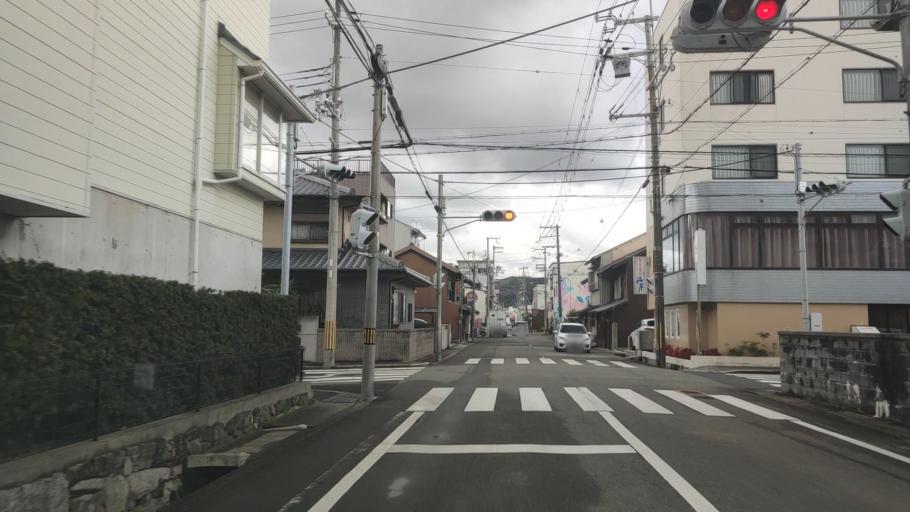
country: JP
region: Hyogo
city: Sumoto
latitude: 34.3413
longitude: 134.9002
